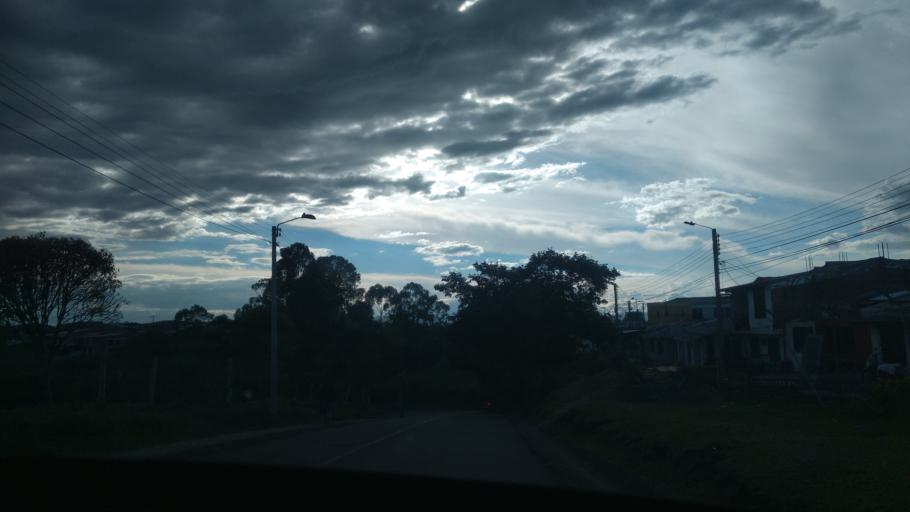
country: CO
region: Cauca
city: Popayan
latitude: 2.4874
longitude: -76.5771
